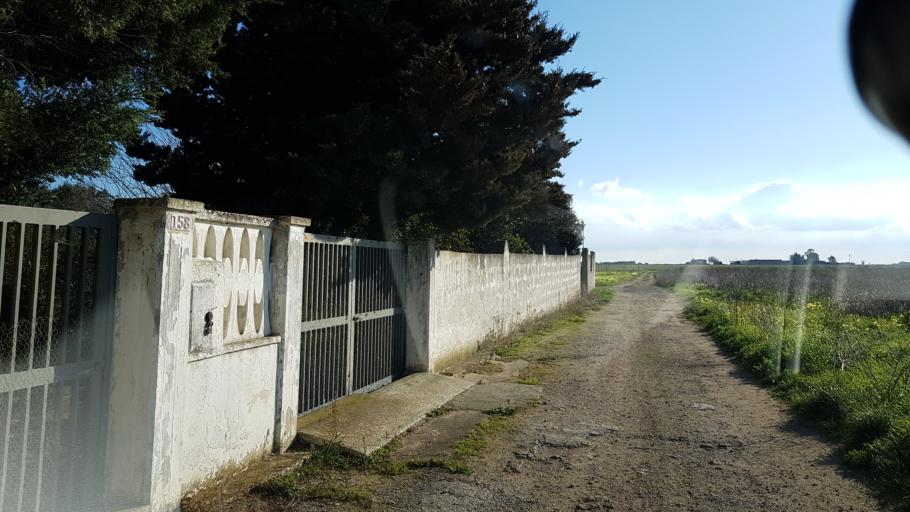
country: IT
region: Apulia
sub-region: Provincia di Brindisi
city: Tuturano
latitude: 40.5406
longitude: 17.9586
